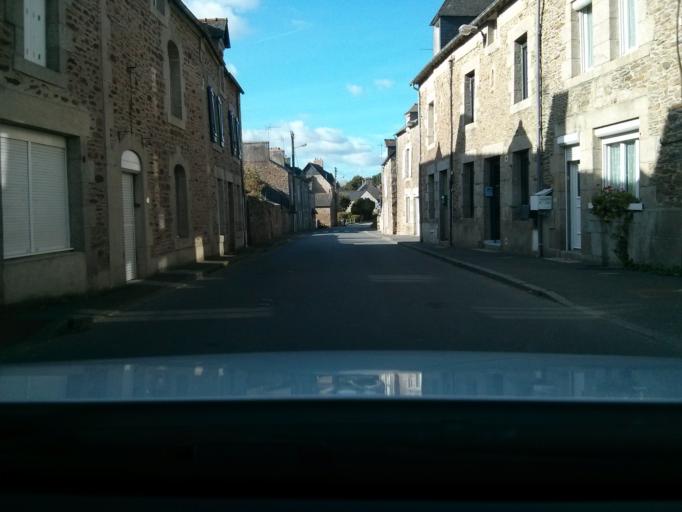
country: FR
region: Brittany
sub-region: Departement des Cotes-d'Armor
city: Pleslin-Trigavou
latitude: 48.5267
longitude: -2.0806
